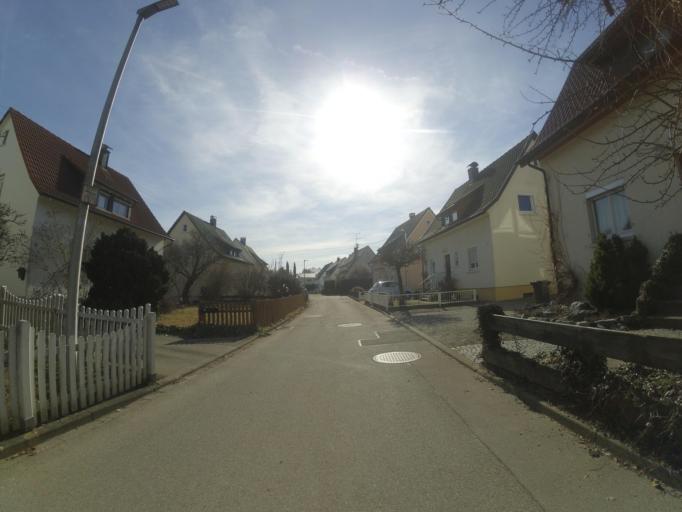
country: DE
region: Baden-Wuerttemberg
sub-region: Tuebingen Region
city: Meckenbeuren
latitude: 47.6941
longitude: 9.5578
